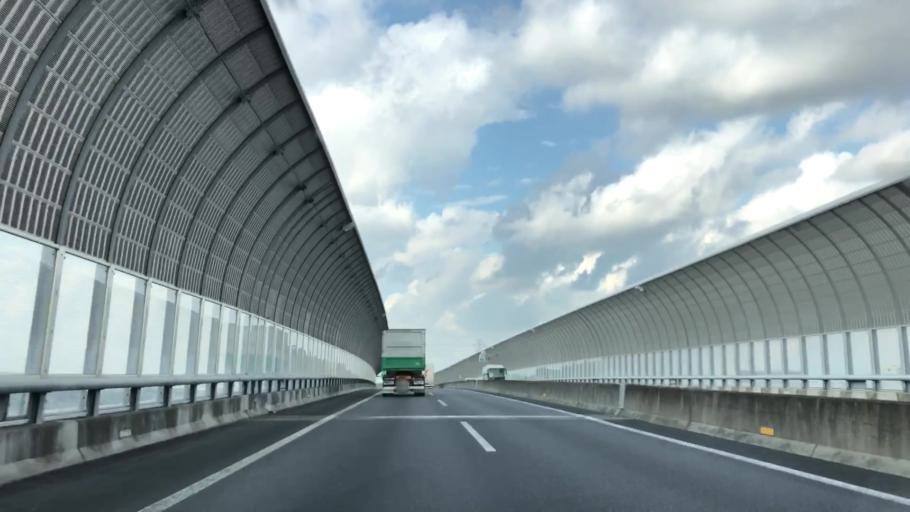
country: JP
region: Saitama
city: Yashio-shi
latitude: 35.8173
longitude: 139.8744
